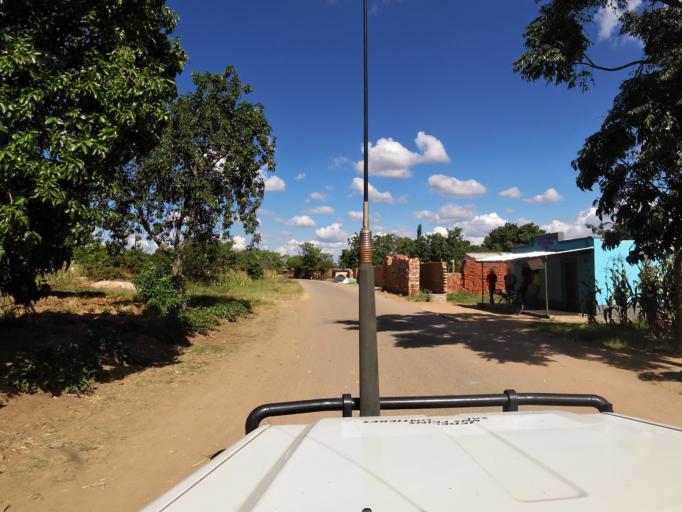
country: ZW
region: Harare
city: Epworth
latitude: -17.8707
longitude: 31.1368
